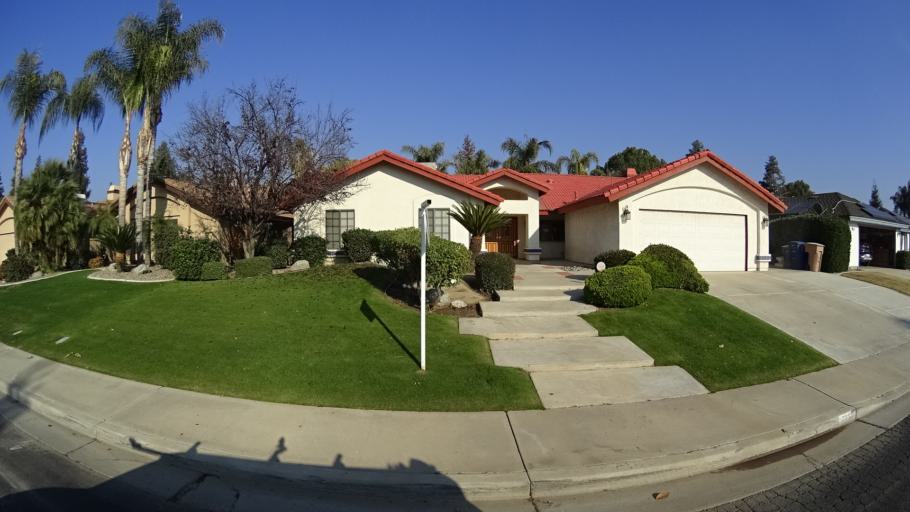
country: US
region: California
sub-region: Kern County
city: Greenacres
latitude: 35.3314
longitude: -119.1077
